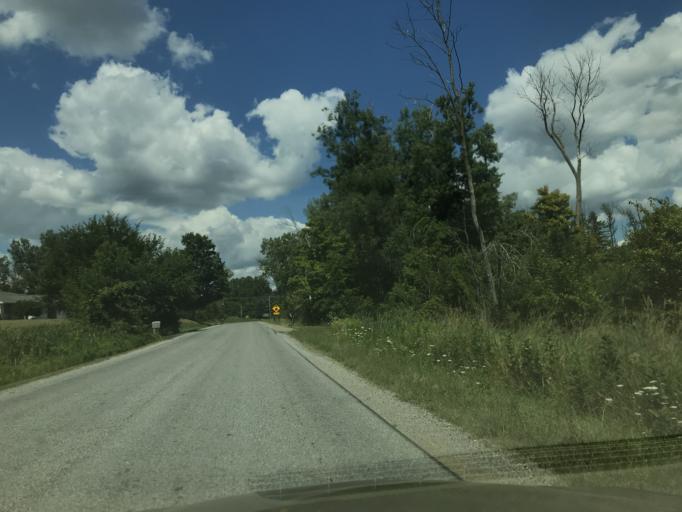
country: US
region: Michigan
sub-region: Ingham County
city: Holt
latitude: 42.6380
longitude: -84.5628
